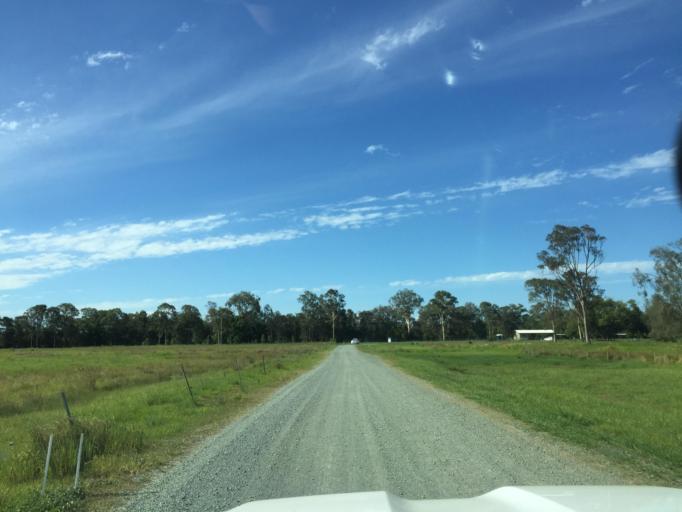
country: AU
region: Queensland
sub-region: Moreton Bay
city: Morayfield
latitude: -27.1087
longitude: 152.9930
